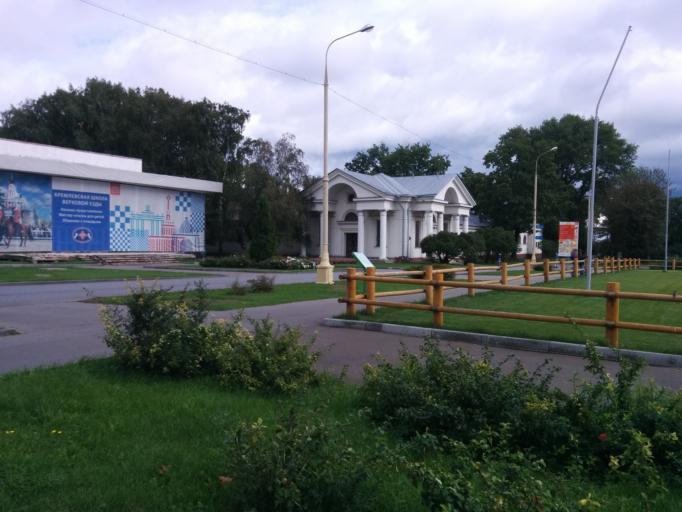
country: RU
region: Moscow
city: Ostankinskiy
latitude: 55.8377
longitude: 37.6227
